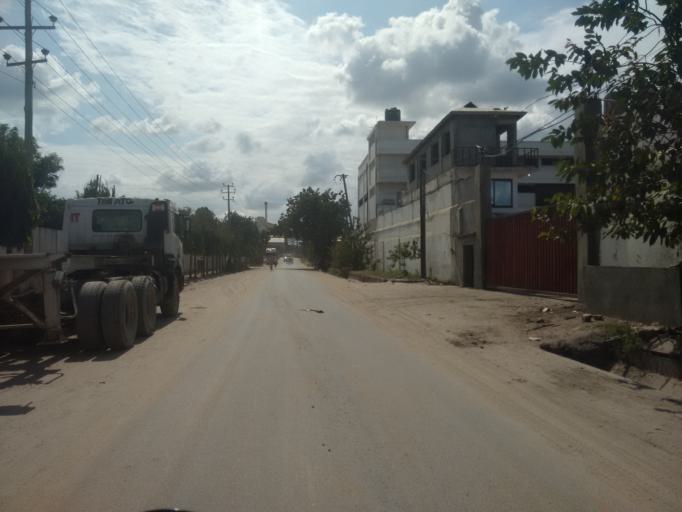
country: TZ
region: Dar es Salaam
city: Dar es Salaam
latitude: -6.8466
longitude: 39.2553
